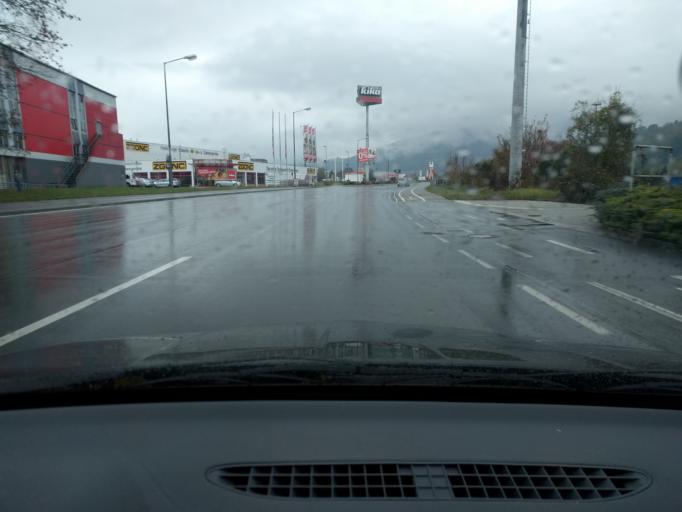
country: AT
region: Styria
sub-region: Politischer Bezirk Leoben
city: Proleb
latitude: 47.3849
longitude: 15.1256
